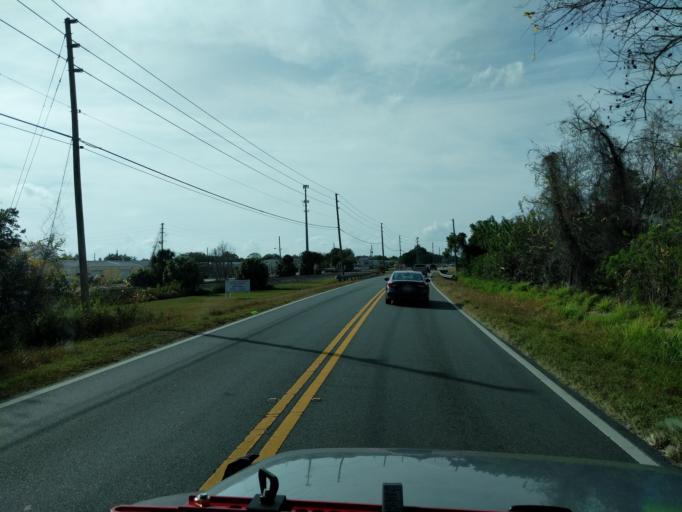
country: US
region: Florida
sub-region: Lake County
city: Tavares
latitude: 28.8038
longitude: -81.6887
